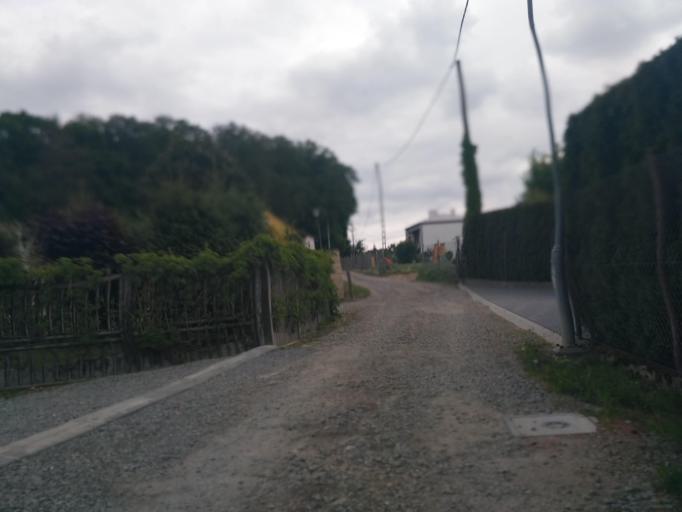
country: PL
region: Subcarpathian Voivodeship
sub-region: Powiat krosnienski
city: Odrzykon
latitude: 49.7245
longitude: 21.7065
